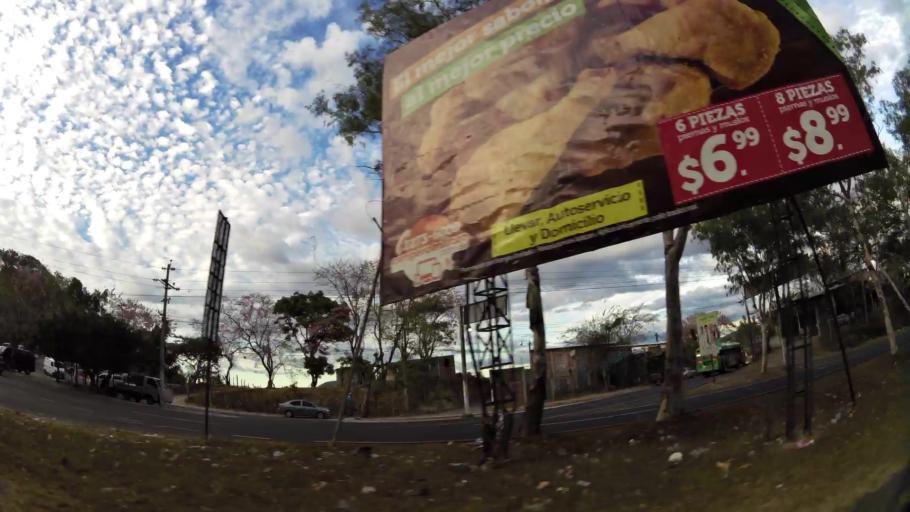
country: SV
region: Cuscatlan
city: Cojutepeque
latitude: 13.7295
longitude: -88.8896
